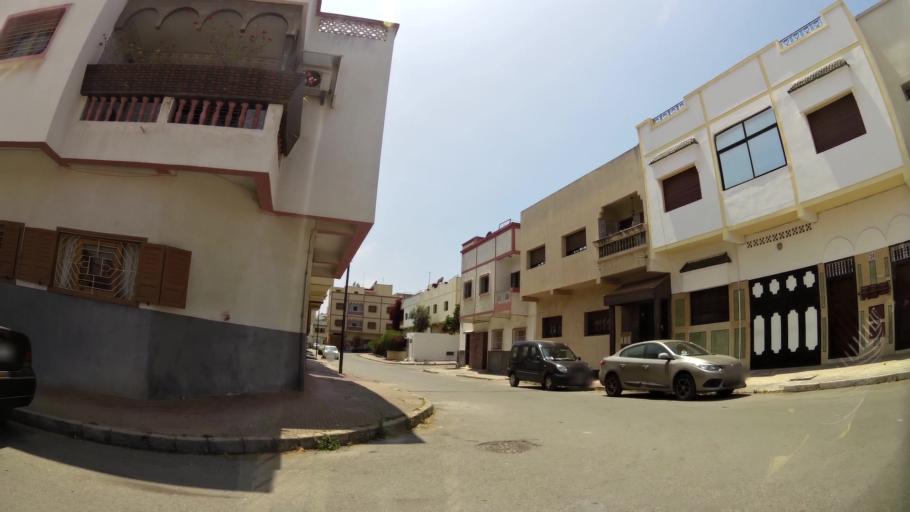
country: MA
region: Rabat-Sale-Zemmour-Zaer
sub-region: Skhirate-Temara
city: Temara
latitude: 33.9774
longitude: -6.8912
